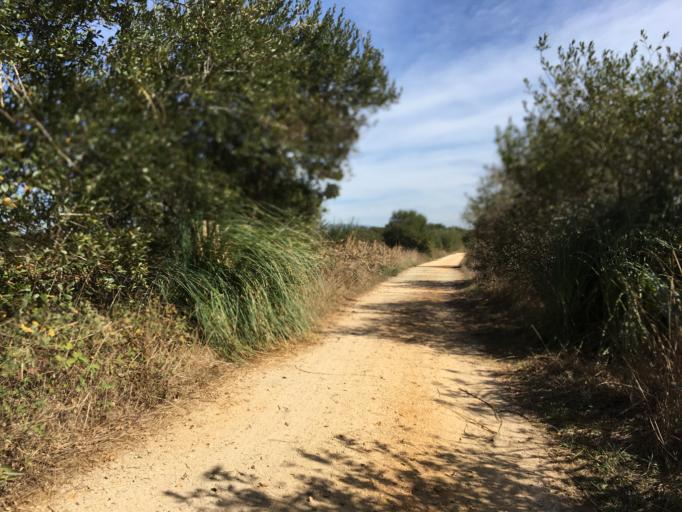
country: PT
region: Aveiro
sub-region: Estarreja
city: Estarreja
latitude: 40.7333
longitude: -8.5821
